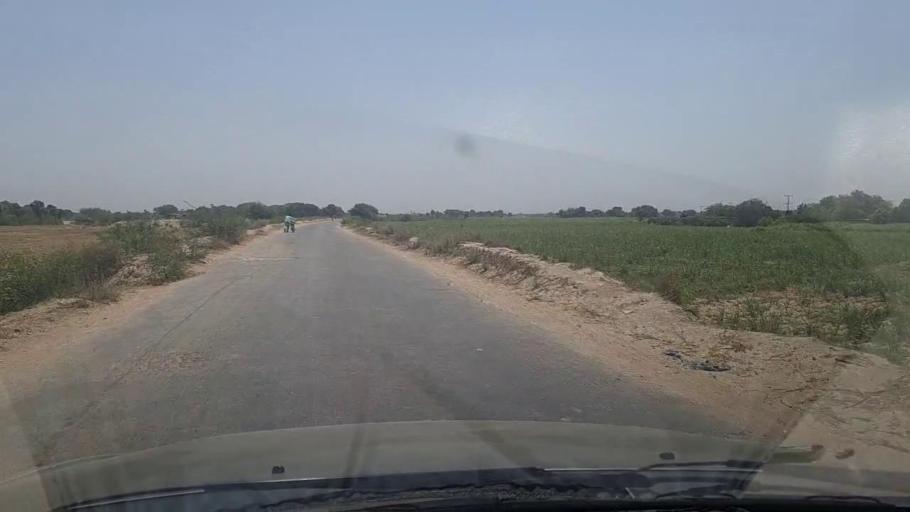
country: PK
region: Sindh
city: Chambar
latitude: 25.2697
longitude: 68.6366
